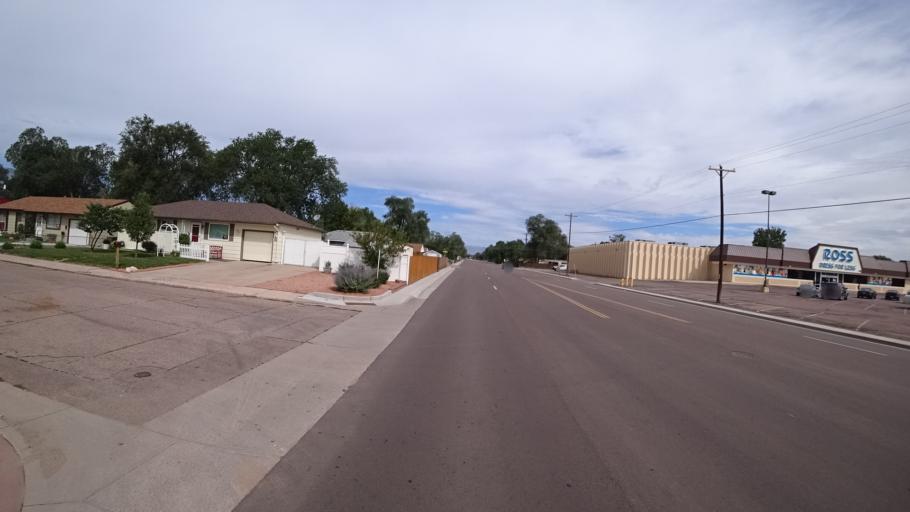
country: US
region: Colorado
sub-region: El Paso County
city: Security-Widefield
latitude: 38.7533
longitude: -104.7429
